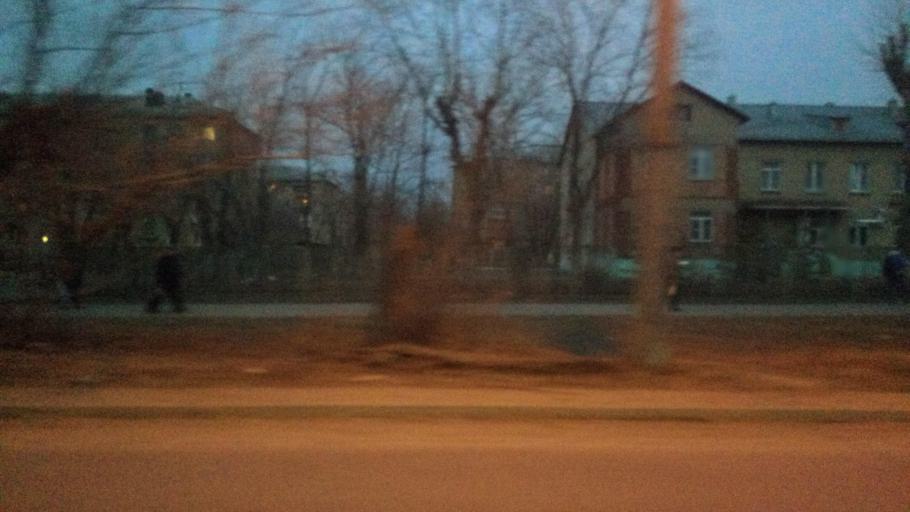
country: RU
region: Chelyabinsk
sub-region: Gorod Chelyabinsk
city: Chelyabinsk
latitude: 55.1686
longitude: 61.4612
